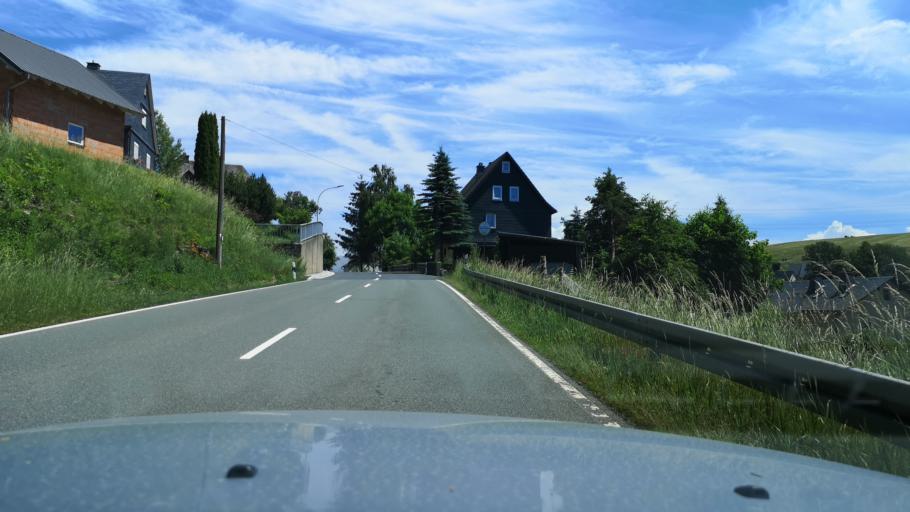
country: DE
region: Bavaria
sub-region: Upper Franconia
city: Tschirn
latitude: 50.3957
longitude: 11.4476
